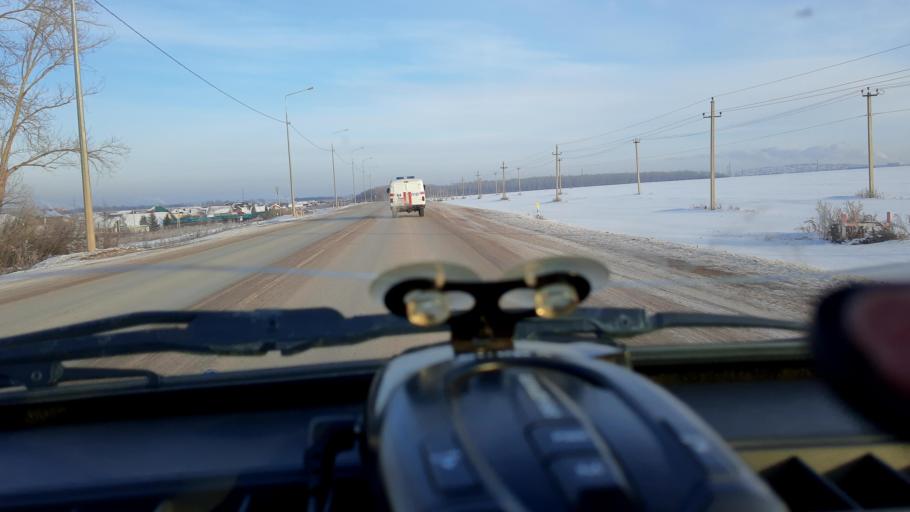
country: RU
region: Bashkortostan
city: Avdon
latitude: 54.6058
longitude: 55.8561
